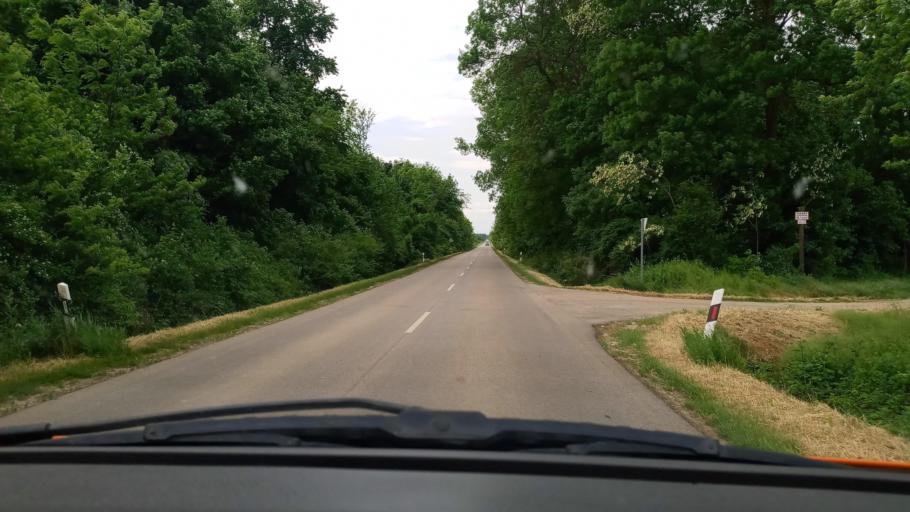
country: HU
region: Baranya
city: Vajszlo
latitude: 45.9263
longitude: 18.0626
